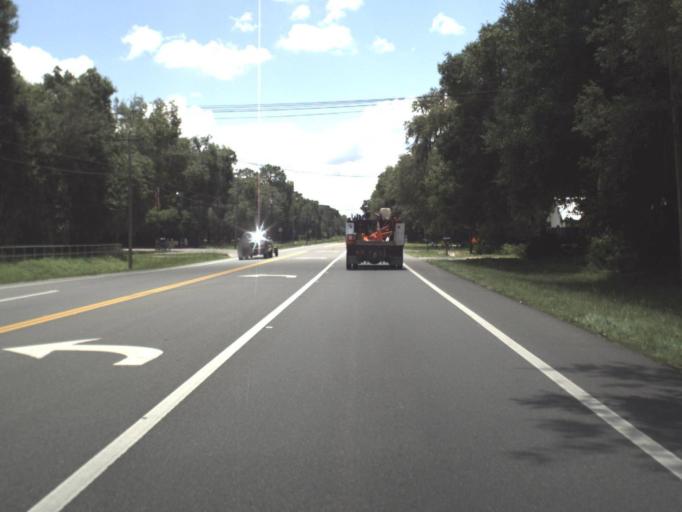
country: US
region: Florida
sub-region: Clay County
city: Keystone Heights
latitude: 29.7709
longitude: -82.0110
